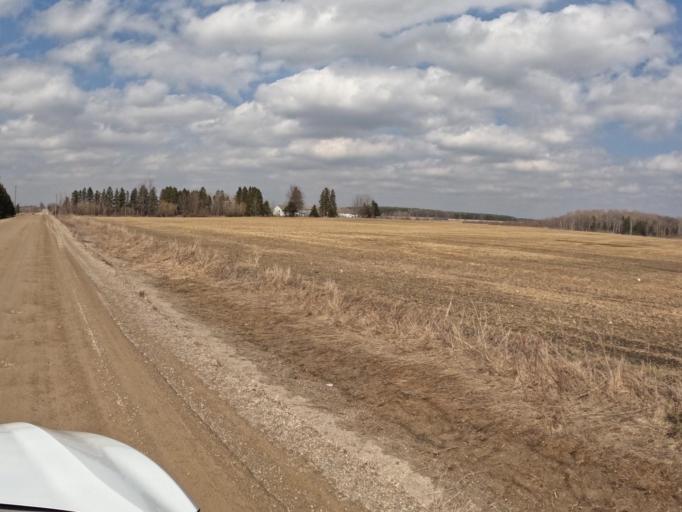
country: CA
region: Ontario
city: Shelburne
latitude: 43.9738
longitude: -80.2677
